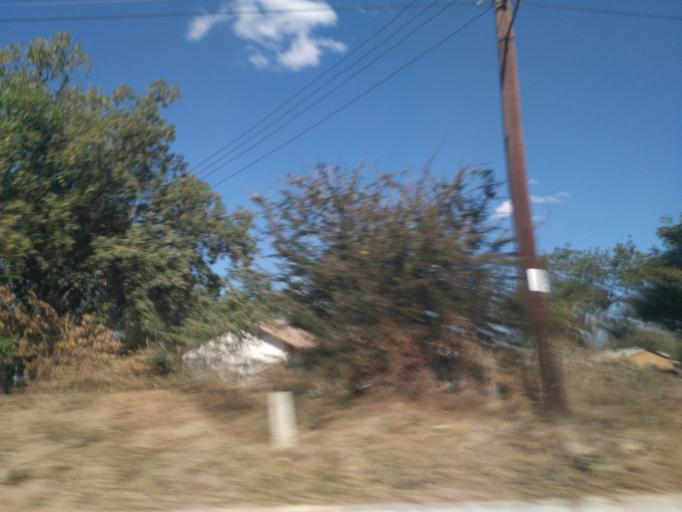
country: TZ
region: Dodoma
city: Dodoma
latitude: -6.1868
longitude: 35.7416
